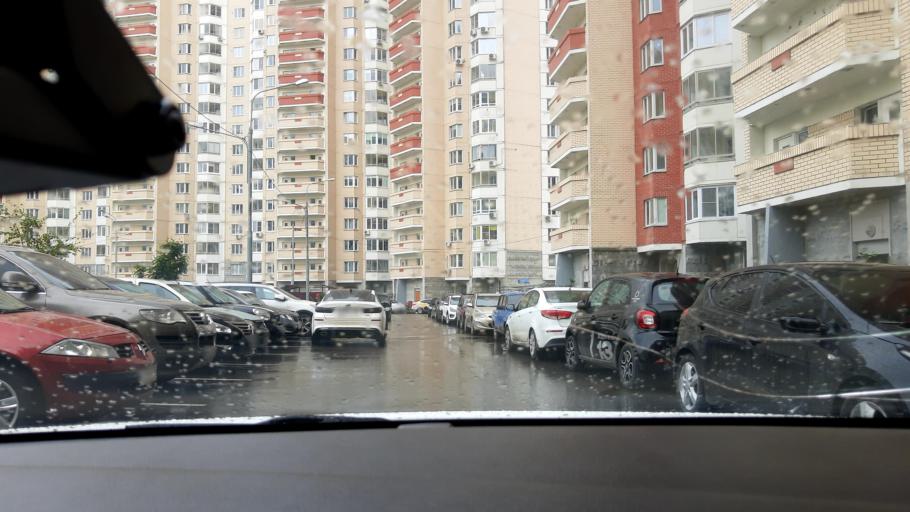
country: RU
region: Moscow
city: Khimki
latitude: 55.8762
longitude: 37.3885
